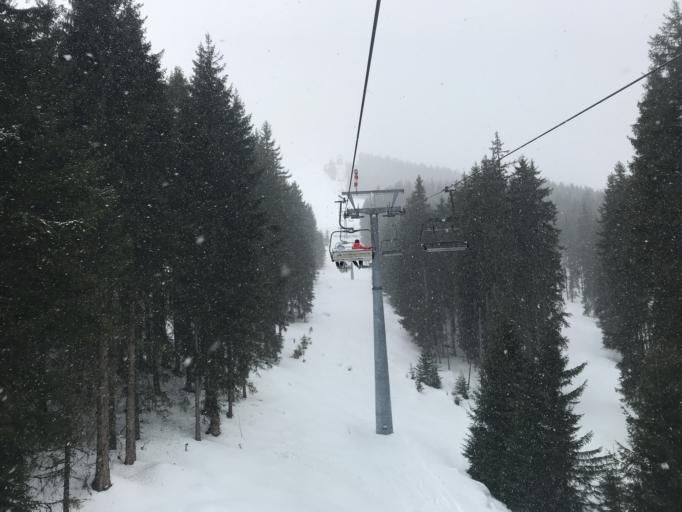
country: AT
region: Salzburg
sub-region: Politischer Bezirk Zell am See
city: Zell am See
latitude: 47.3155
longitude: 12.7596
